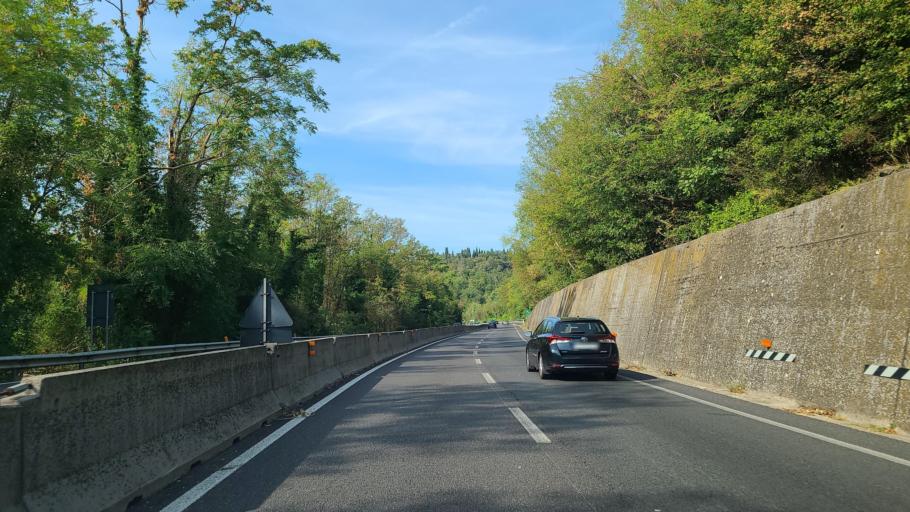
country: IT
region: Tuscany
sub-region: Province of Florence
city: San Casciano in Val di Pesa
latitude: 43.6587
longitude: 11.2023
